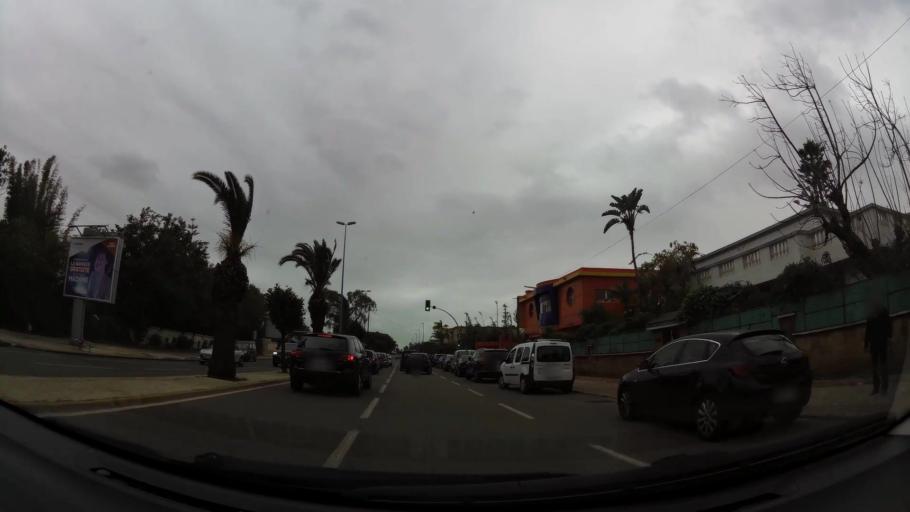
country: MA
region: Grand Casablanca
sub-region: Casablanca
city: Casablanca
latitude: 33.5942
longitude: -7.6545
